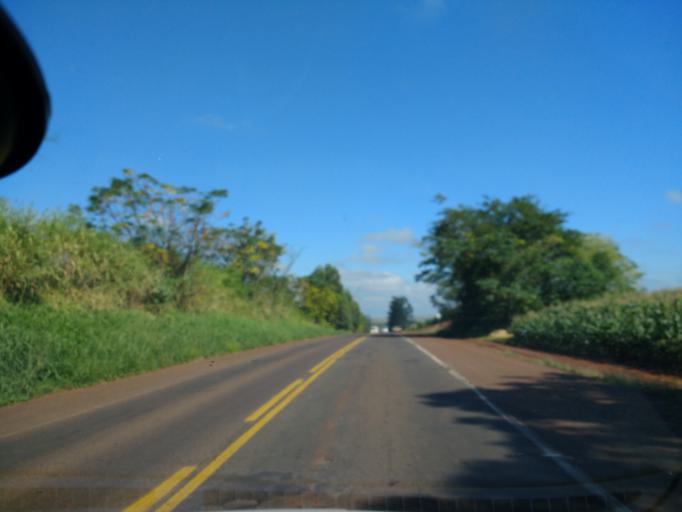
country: BR
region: Parana
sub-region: Paicandu
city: Paicandu
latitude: -23.5085
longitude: -52.1688
